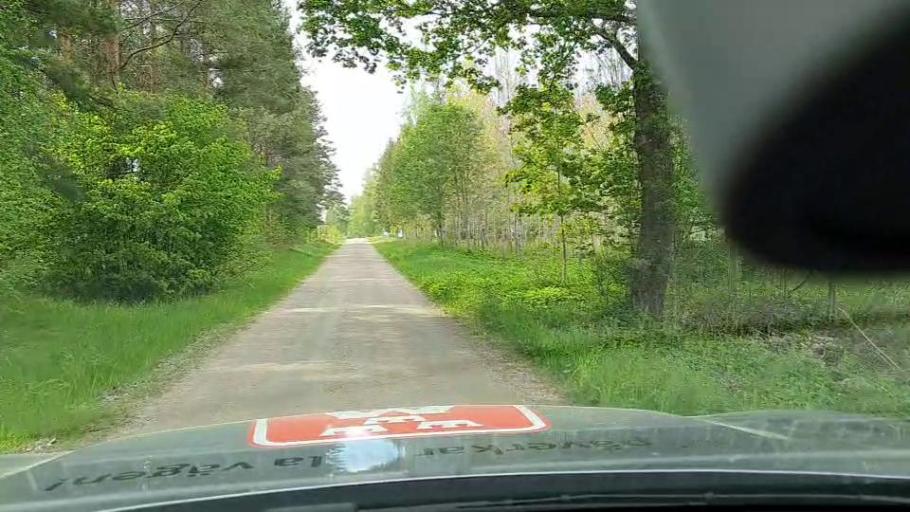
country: SE
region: Soedermanland
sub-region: Strangnas Kommun
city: Akers Styckebruk
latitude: 59.2479
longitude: 16.9336
